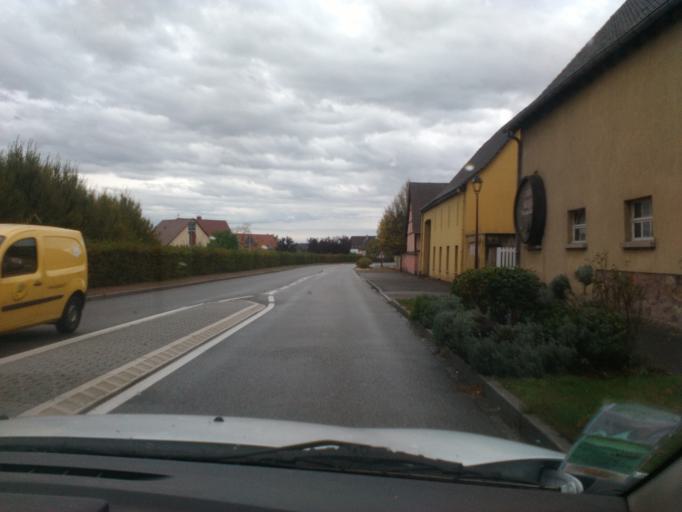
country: FR
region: Alsace
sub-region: Departement du Haut-Rhin
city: Ammerschwihr
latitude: 48.1276
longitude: 7.2828
